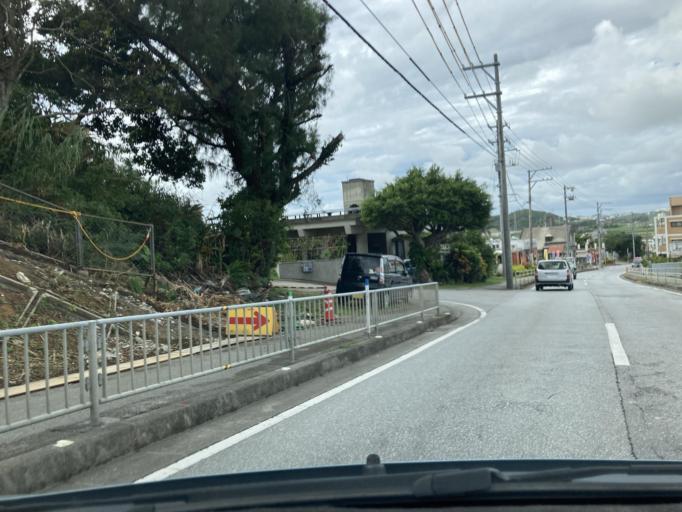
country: JP
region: Okinawa
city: Tomigusuku
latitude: 26.1792
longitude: 127.7435
